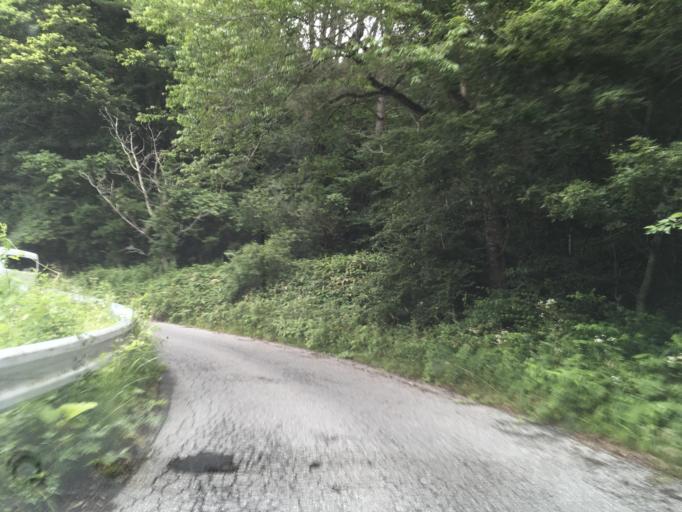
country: JP
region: Iwate
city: Ofunato
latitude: 38.8826
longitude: 141.4683
